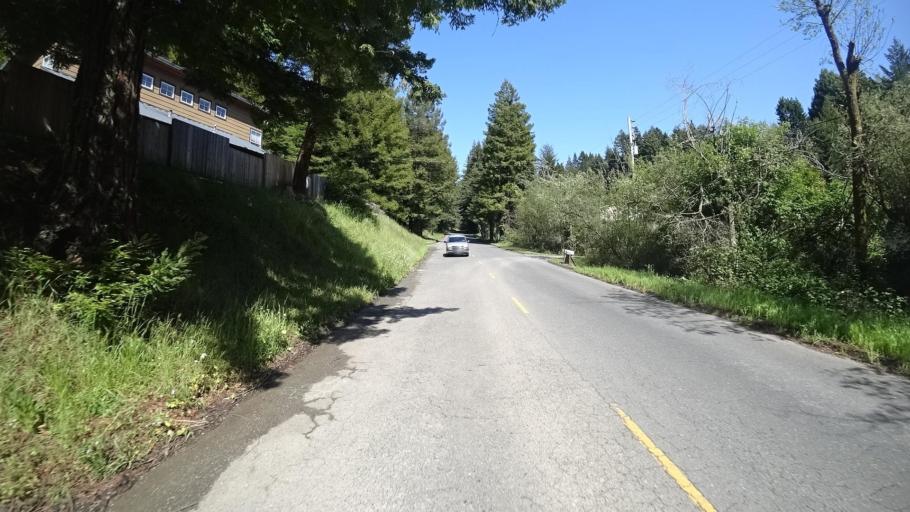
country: US
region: California
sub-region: Humboldt County
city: Hydesville
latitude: 40.5689
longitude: -124.1154
